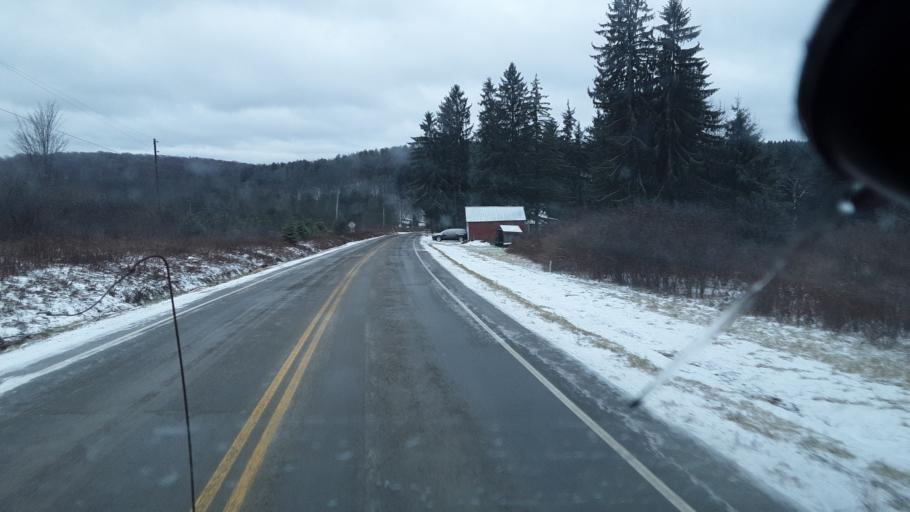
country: US
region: New York
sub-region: Allegany County
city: Friendship
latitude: 42.2357
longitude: -78.1425
